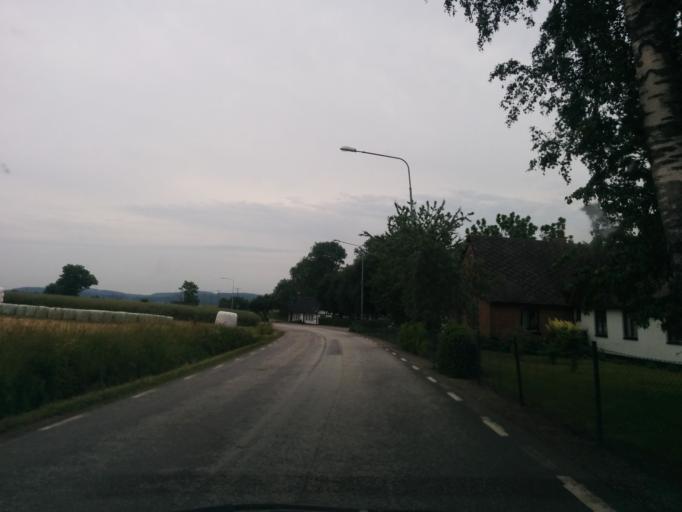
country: SE
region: Skane
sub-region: Lunds Kommun
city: Genarp
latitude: 55.6411
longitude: 13.3545
